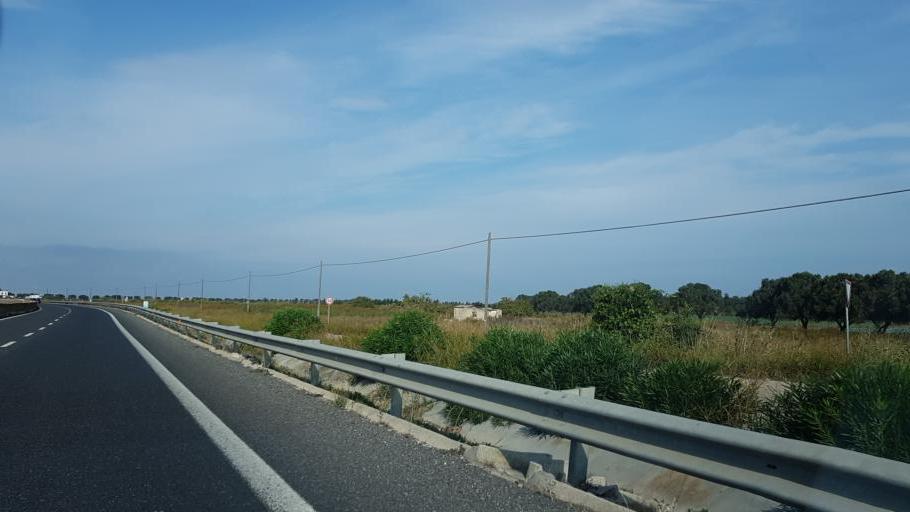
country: IT
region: Apulia
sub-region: Provincia di Brindisi
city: Brindisi
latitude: 40.6587
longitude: 17.8935
